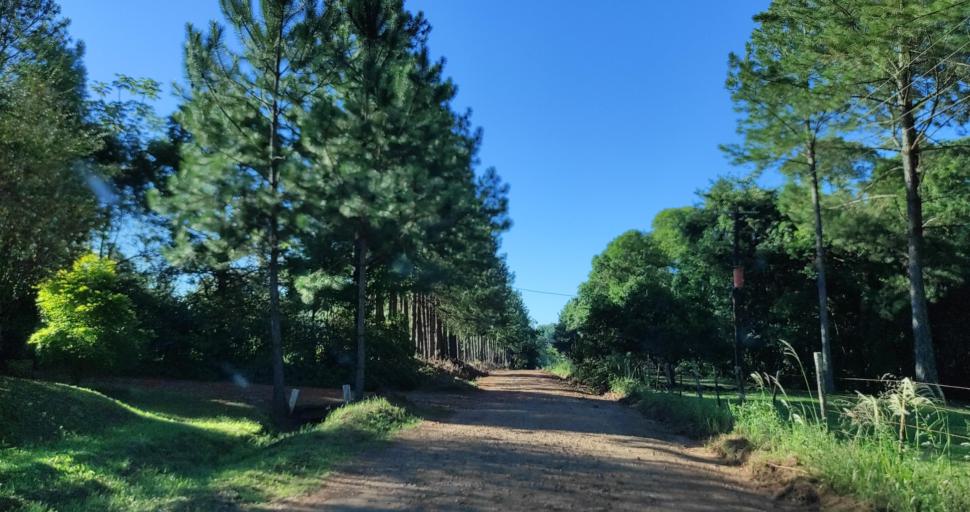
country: AR
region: Misiones
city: Puerto Rico
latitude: -26.8410
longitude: -55.0024
